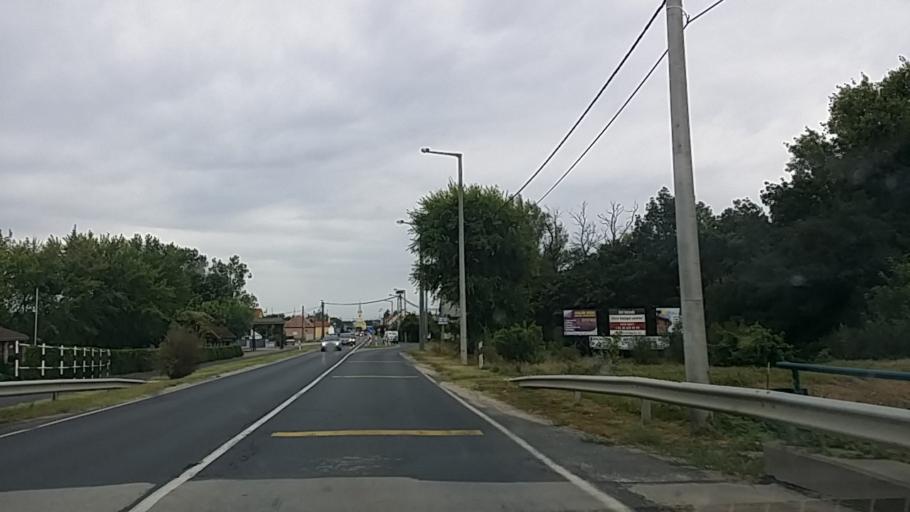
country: HU
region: Gyor-Moson-Sopron
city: Kapuvar
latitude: 47.5883
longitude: 16.9897
